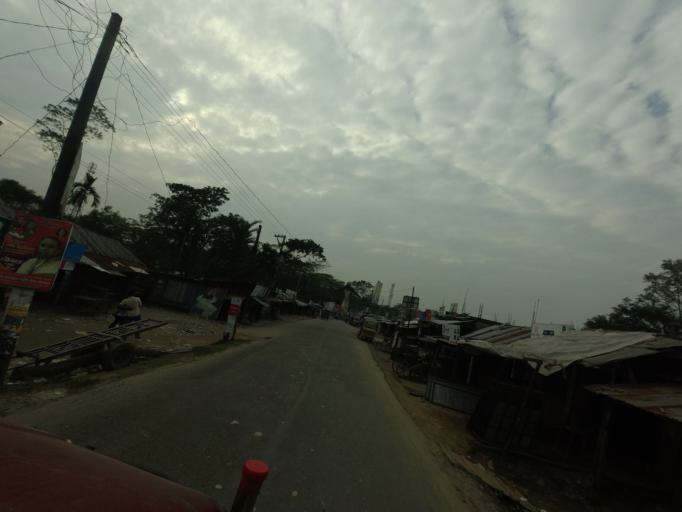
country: BD
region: Barisal
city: Nalchiti
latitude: 22.4537
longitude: 90.3418
